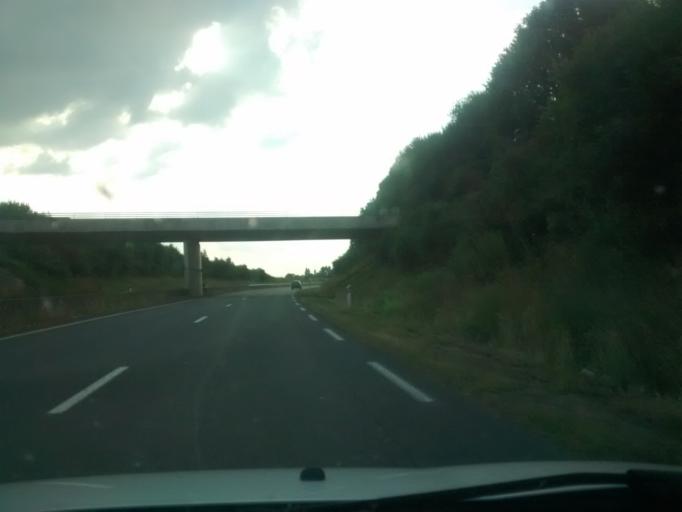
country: FR
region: Brittany
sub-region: Departement des Cotes-d'Armor
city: Begard
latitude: 48.6179
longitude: -3.3051
